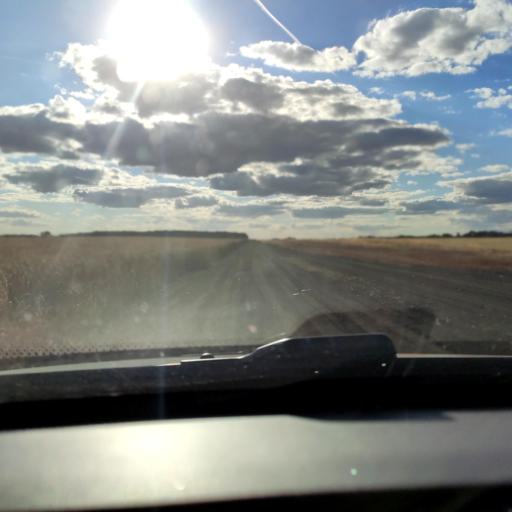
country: RU
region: Voronezj
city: Verkhnyaya Khava
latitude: 51.6086
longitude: 39.8339
